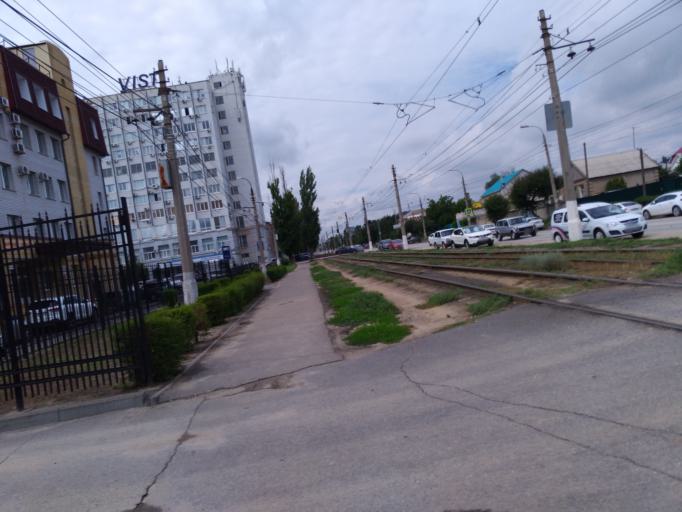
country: RU
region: Volgograd
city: Volgograd
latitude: 48.7159
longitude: 44.4887
